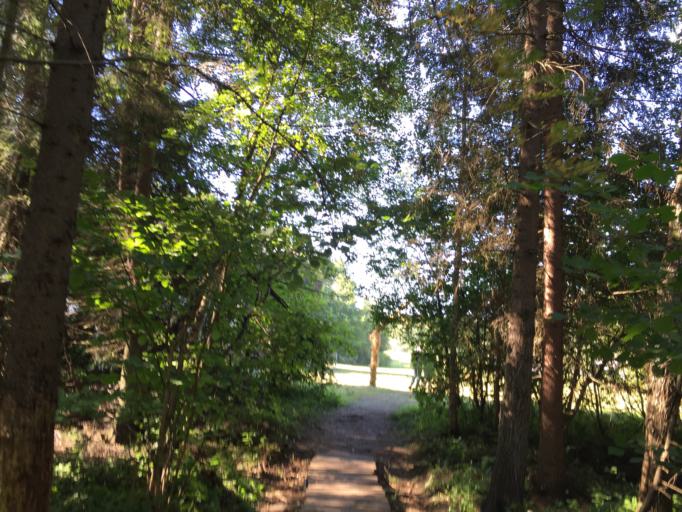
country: LT
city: Zarasai
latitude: 55.7917
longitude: 25.9615
